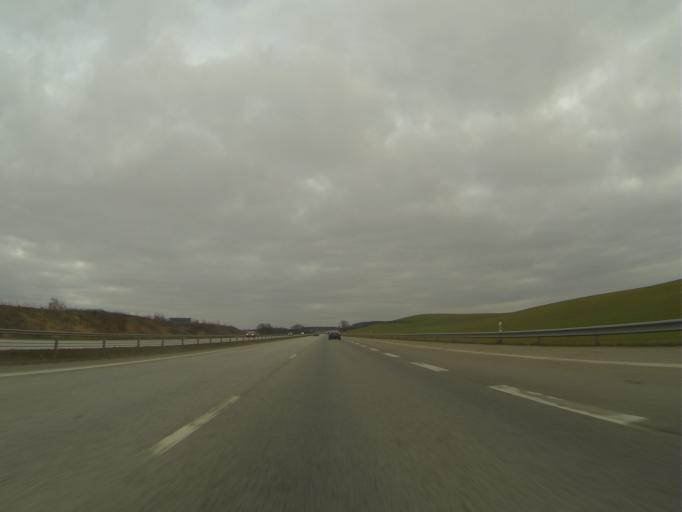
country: SE
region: Skane
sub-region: Malmo
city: Oxie
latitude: 55.5534
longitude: 13.1099
